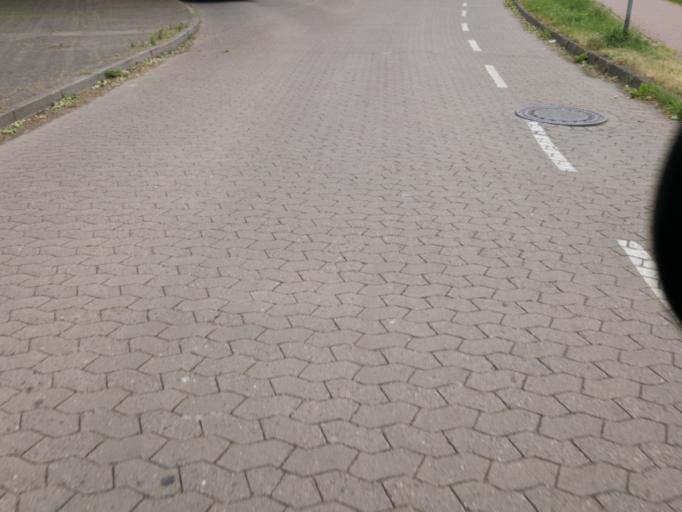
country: DE
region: Lower Saxony
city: Stolzenau
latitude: 52.5105
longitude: 9.0698
